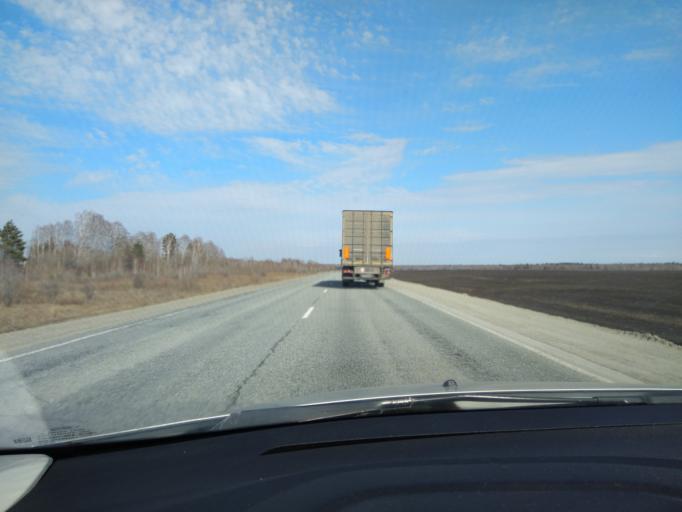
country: RU
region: Sverdlovsk
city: Tugulym
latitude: 57.0725
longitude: 64.6992
